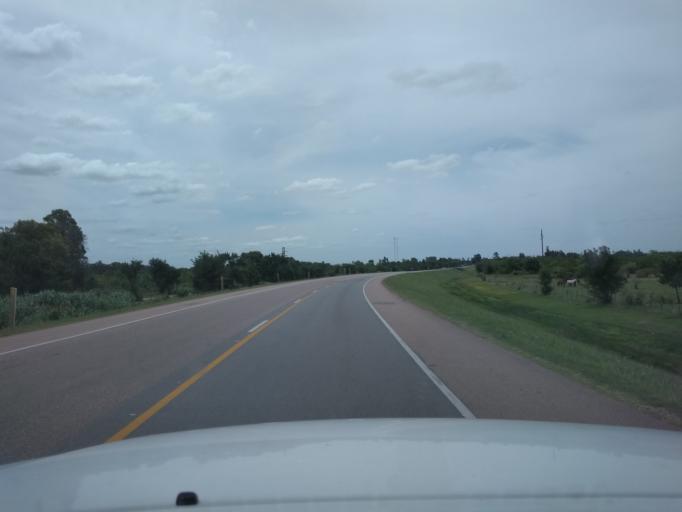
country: UY
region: Canelones
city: Canelones
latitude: -34.5069
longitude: -56.2810
